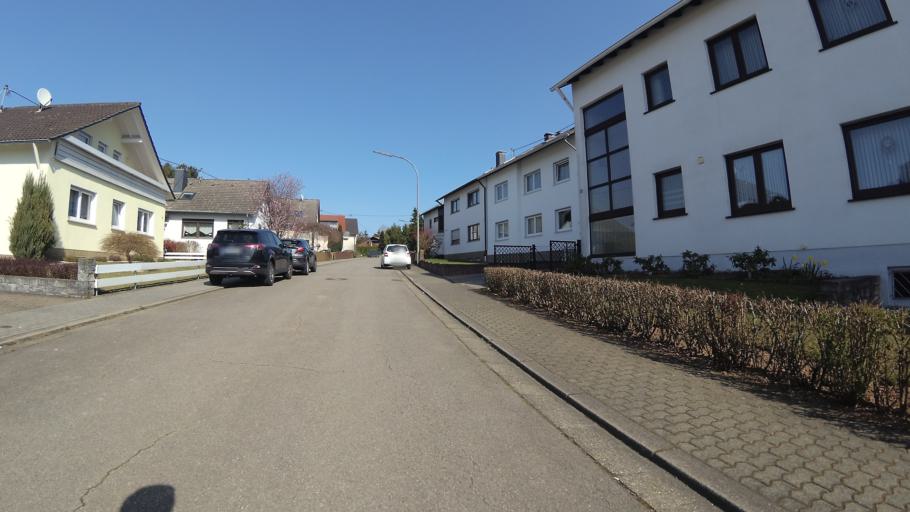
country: DE
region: Saarland
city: Merchweiler
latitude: 49.3468
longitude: 7.0061
